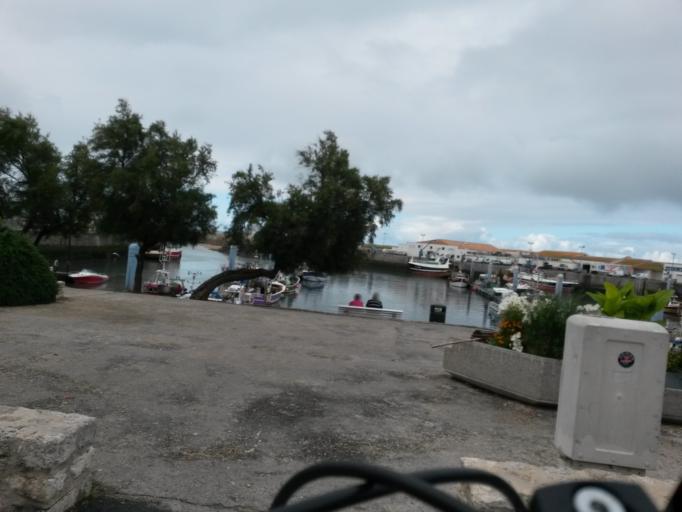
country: FR
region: Poitou-Charentes
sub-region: Departement de la Charente-Maritime
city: Dolus-d'Oleron
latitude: 45.9154
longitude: -1.3275
